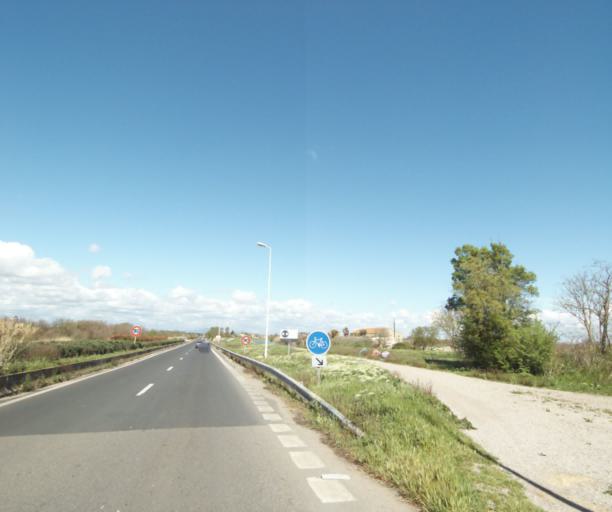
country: FR
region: Languedoc-Roussillon
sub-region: Departement de l'Herault
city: Lattes
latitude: 43.5411
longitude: 3.8974
